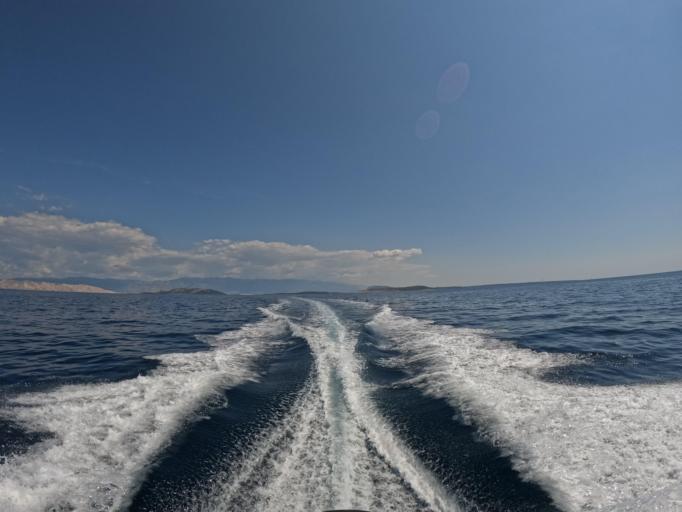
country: HR
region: Primorsko-Goranska
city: Lopar
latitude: 44.8852
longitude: 14.6421
